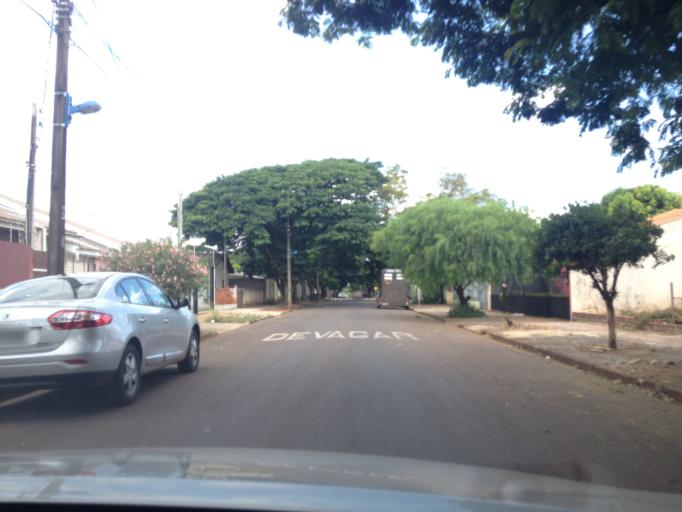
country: BR
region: Parana
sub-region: Sarandi
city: Sarandi
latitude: -23.4386
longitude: -51.8970
